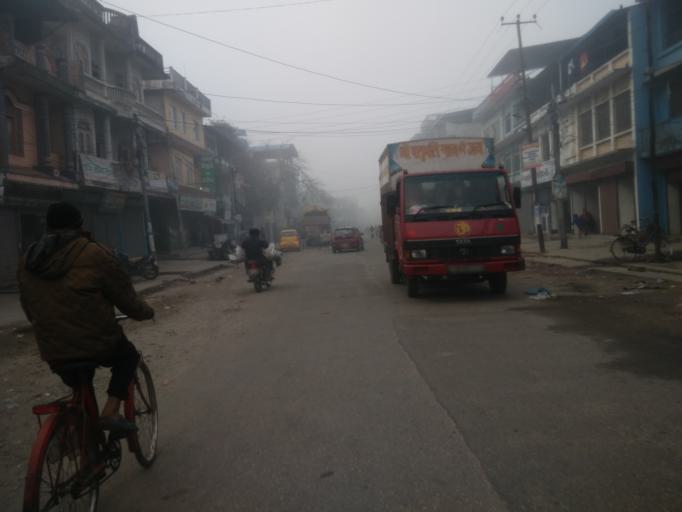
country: NP
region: Central Region
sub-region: Narayani Zone
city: Bharatpur
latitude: 27.6922
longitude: 84.4214
